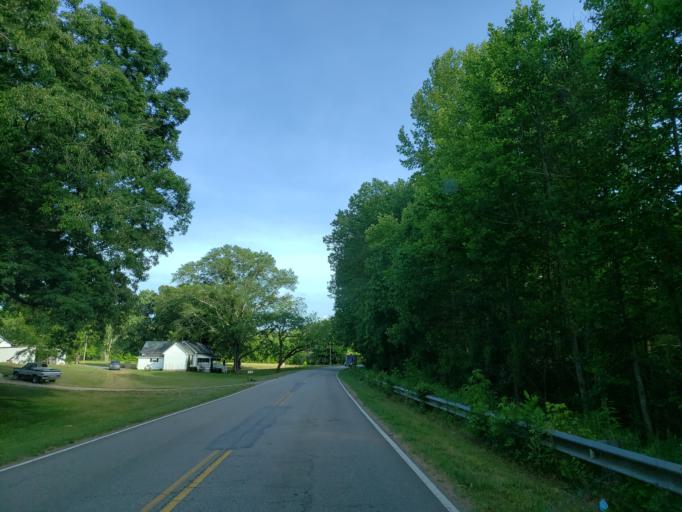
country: US
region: Georgia
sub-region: Carroll County
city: Bowdon
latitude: 33.4863
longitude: -85.3033
